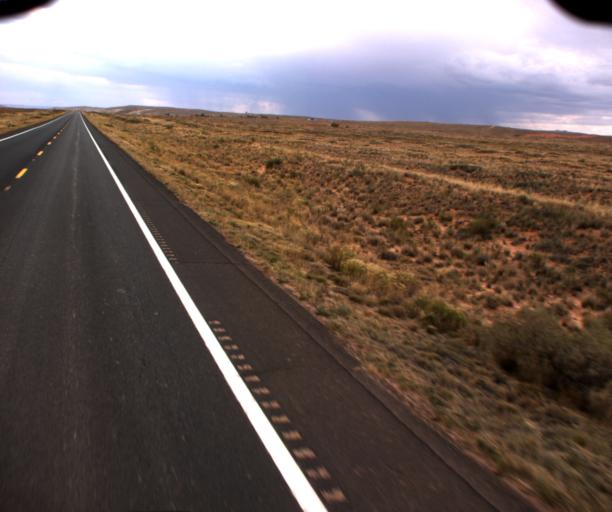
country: US
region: Arizona
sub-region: Coconino County
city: Kaibito
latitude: 36.3653
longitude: -110.8994
